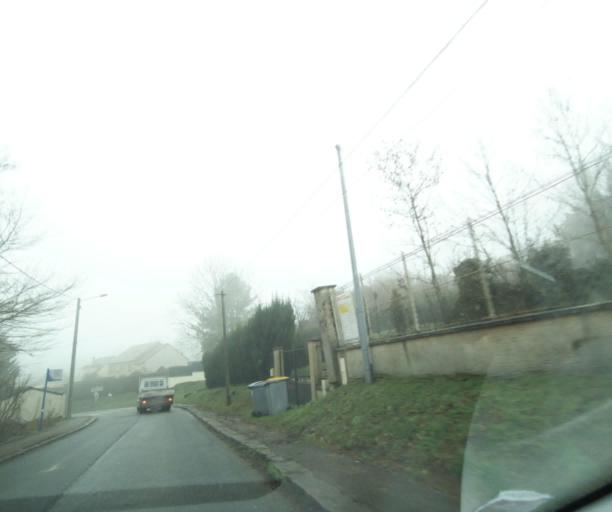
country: FR
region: Ile-de-France
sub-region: Departement de Seine-et-Marne
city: Longperrier
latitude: 49.0518
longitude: 2.6704
